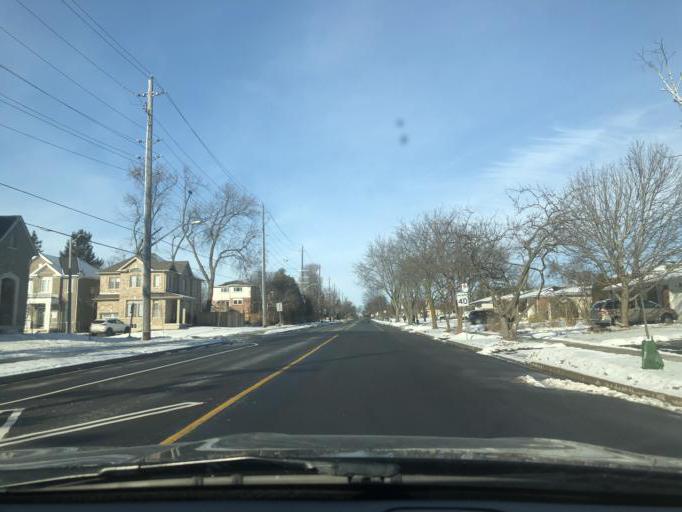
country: CA
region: Ontario
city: Scarborough
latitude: 43.7837
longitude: -79.1491
